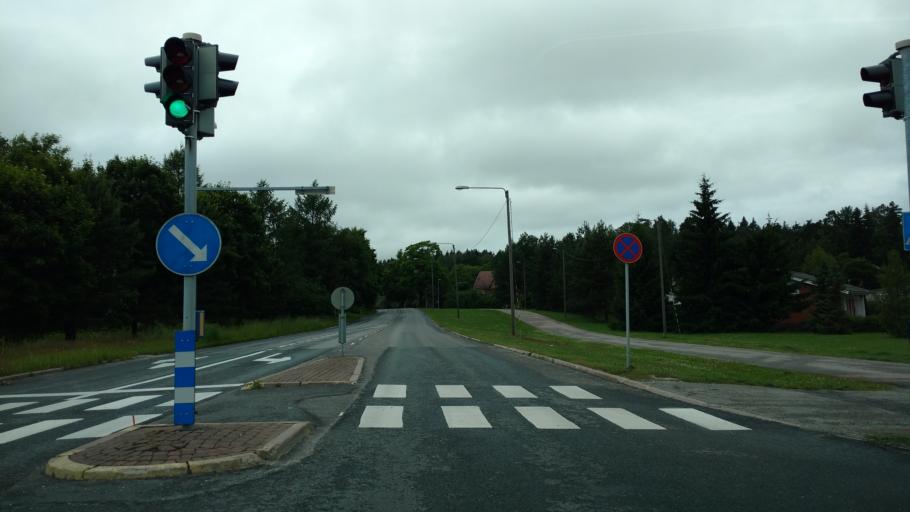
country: FI
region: Varsinais-Suomi
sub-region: Salo
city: Halikko
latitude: 60.3959
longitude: 23.1022
